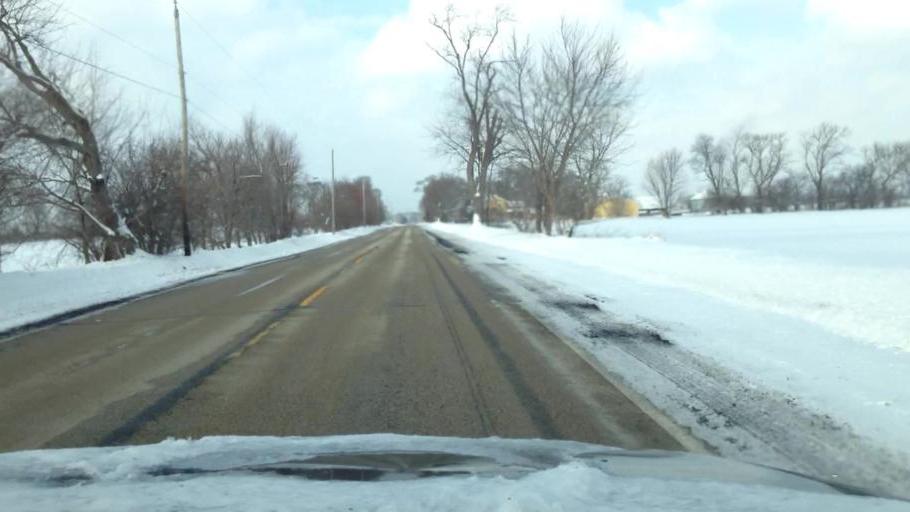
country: US
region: Wisconsin
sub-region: Walworth County
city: East Troy
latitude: 42.7840
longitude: -88.4450
